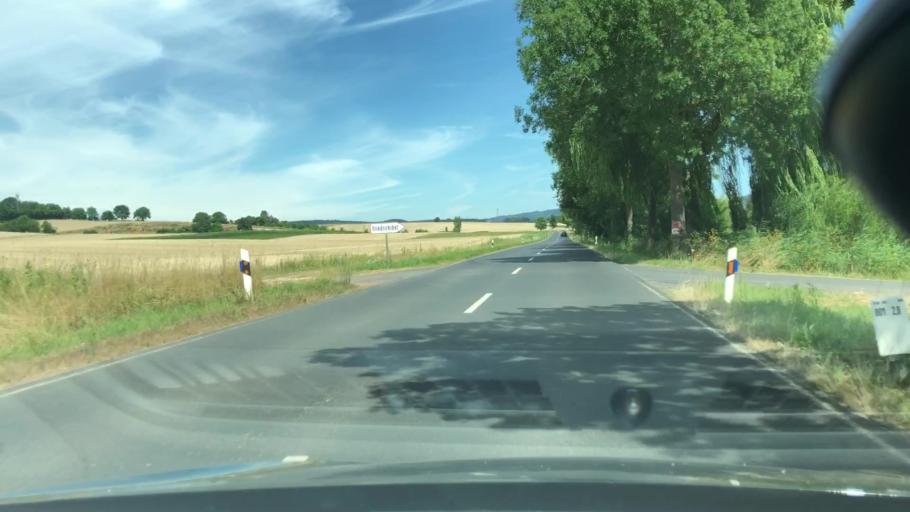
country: DE
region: Hesse
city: Hain-Grundau
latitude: 50.2109
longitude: 9.0936
